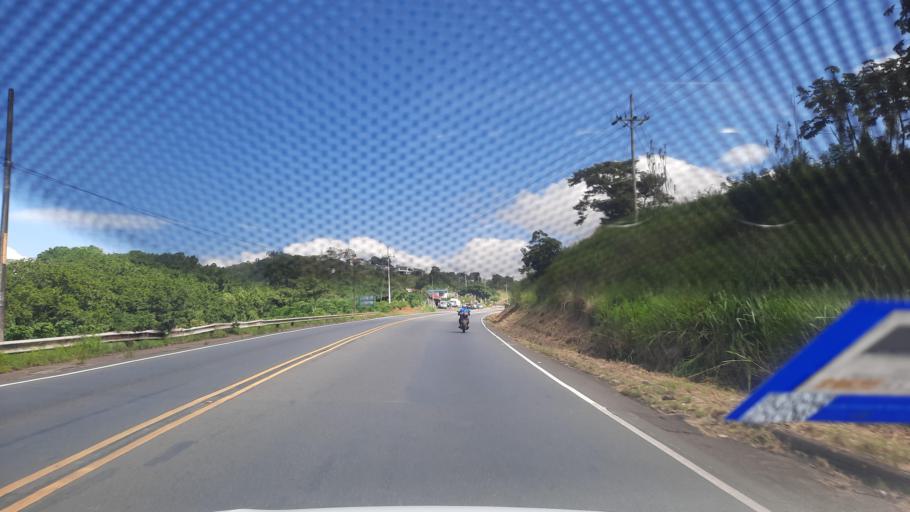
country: CR
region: Alajuela
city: Naranjo
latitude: 10.0666
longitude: -84.3663
